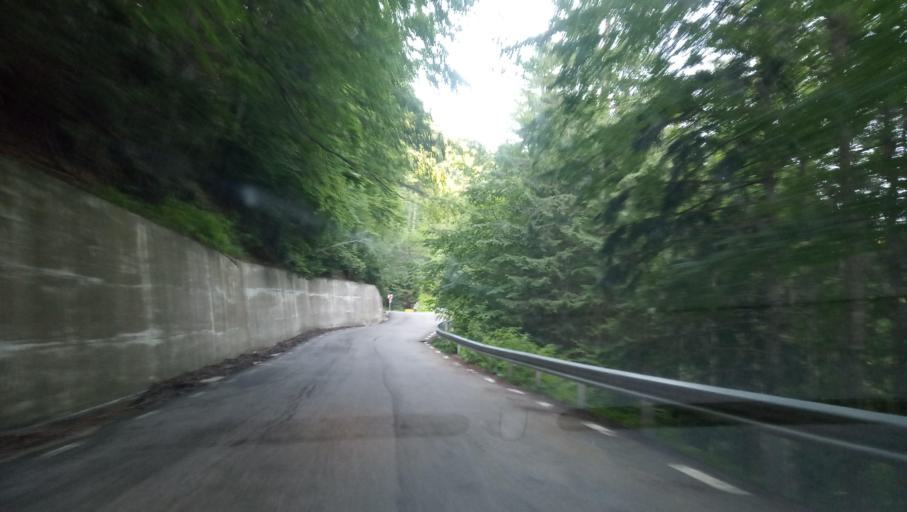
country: RO
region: Prahova
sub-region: Oras Sinaia
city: Sinaia
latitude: 45.3200
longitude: 25.4940
